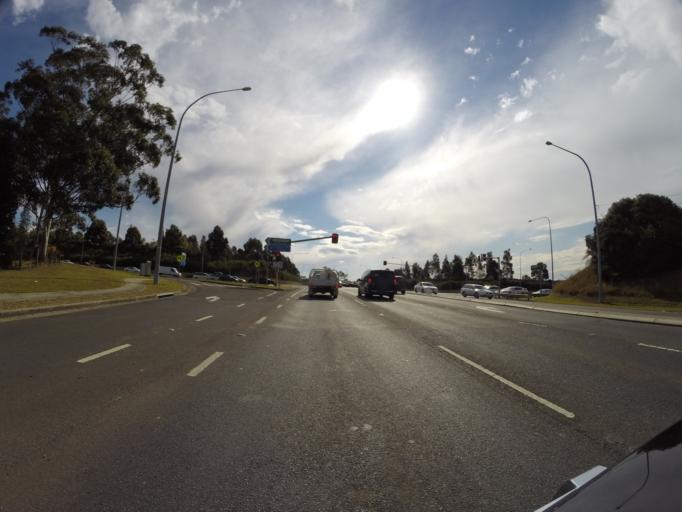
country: AU
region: New South Wales
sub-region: Campbelltown Municipality
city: Campbelltown
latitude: -34.0685
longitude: 150.8028
